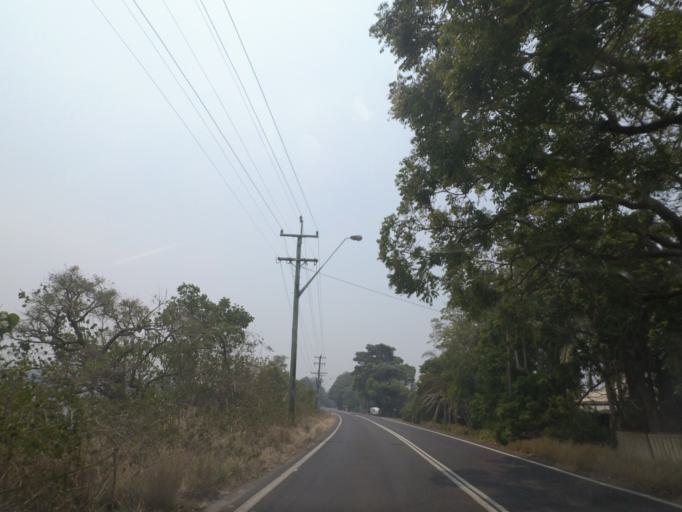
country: AU
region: New South Wales
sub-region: Richmond Valley
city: Evans Head
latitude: -29.0045
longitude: 153.4364
